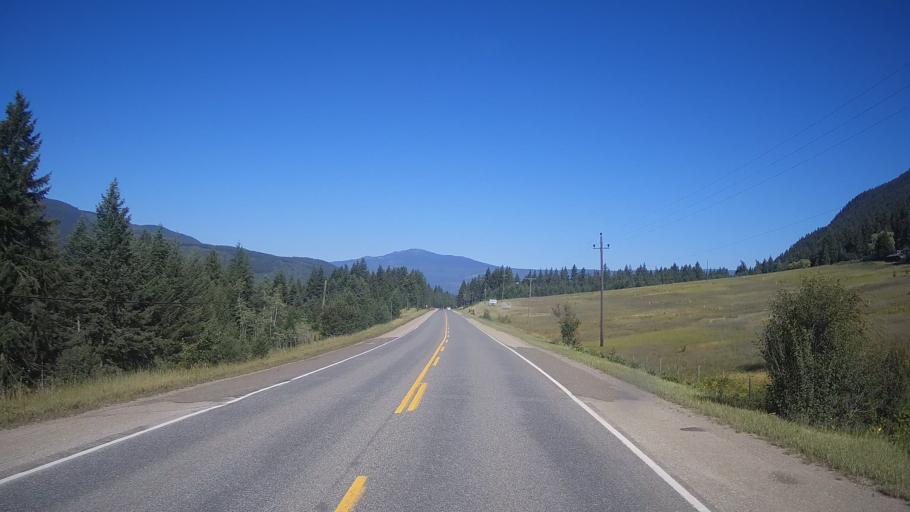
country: CA
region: British Columbia
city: Chase
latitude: 51.6115
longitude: -119.9178
